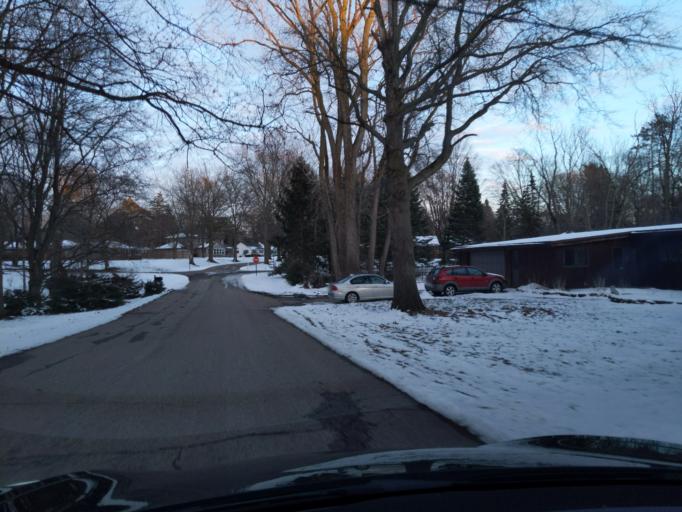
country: US
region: Michigan
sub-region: Ingham County
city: Okemos
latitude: 42.7161
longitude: -84.4407
